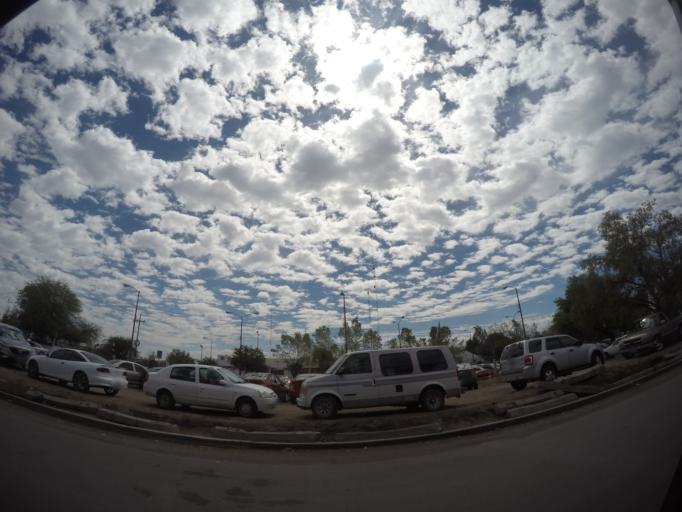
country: MX
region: Guanajuato
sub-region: Leon
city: San Antonio de los Tepetates
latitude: 21.0494
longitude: -101.6898
